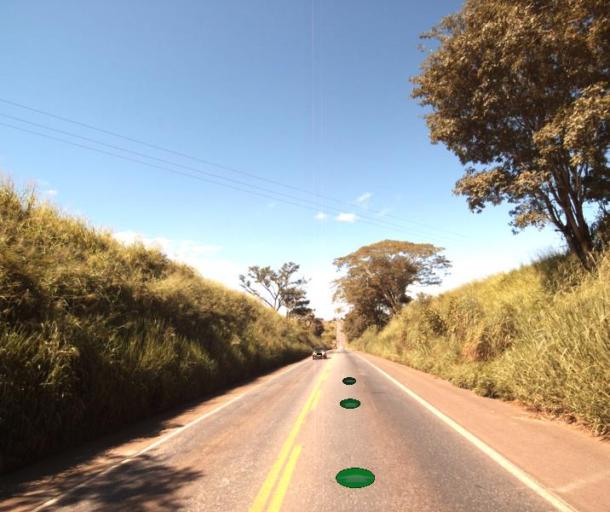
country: BR
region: Goias
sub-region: Rialma
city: Rialma
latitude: -15.3406
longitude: -49.5694
